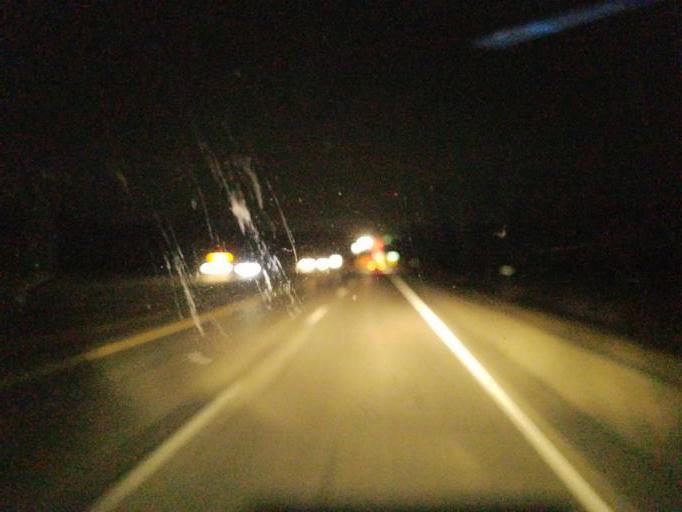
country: US
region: Iowa
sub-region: Dallas County
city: De Soto
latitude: 41.5427
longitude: -93.9888
